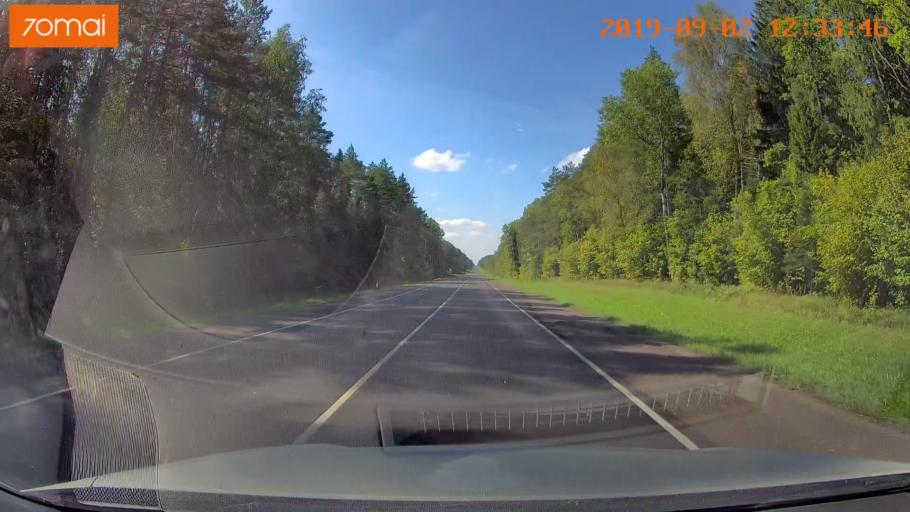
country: RU
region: Smolensk
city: Shumyachi
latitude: 53.8154
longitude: 32.4207
